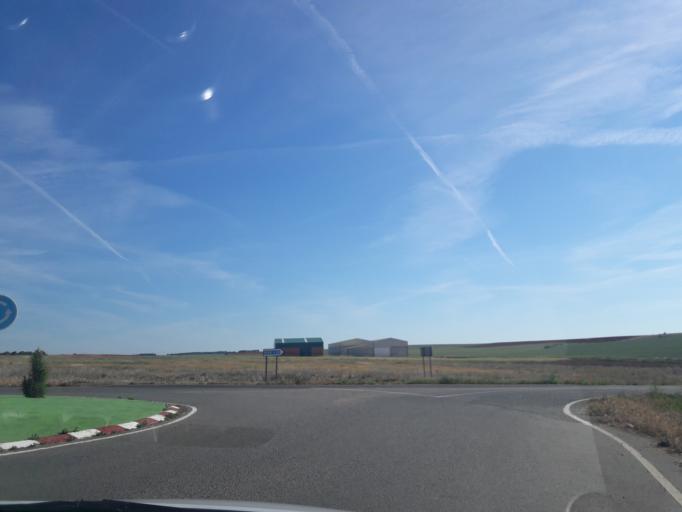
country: ES
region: Castille and Leon
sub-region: Provincia de Salamanca
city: Aldeanueva de Figueroa
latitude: 41.1479
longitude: -5.5208
